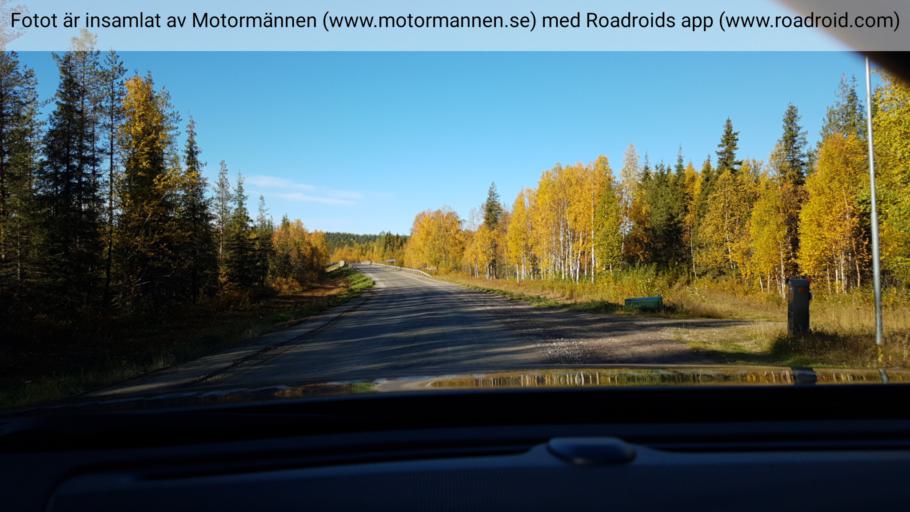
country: SE
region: Norrbotten
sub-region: Alvsbyns Kommun
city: AElvsbyn
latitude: 66.2784
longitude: 21.1056
